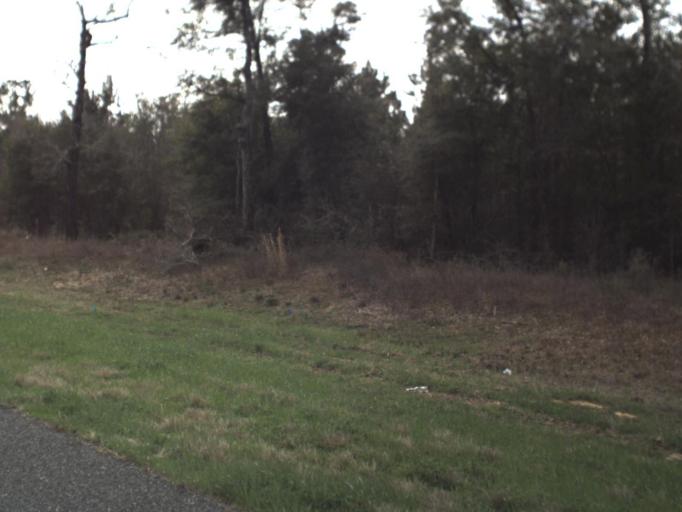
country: US
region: Florida
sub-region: Washington County
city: Chipley
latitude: 30.7424
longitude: -85.3854
